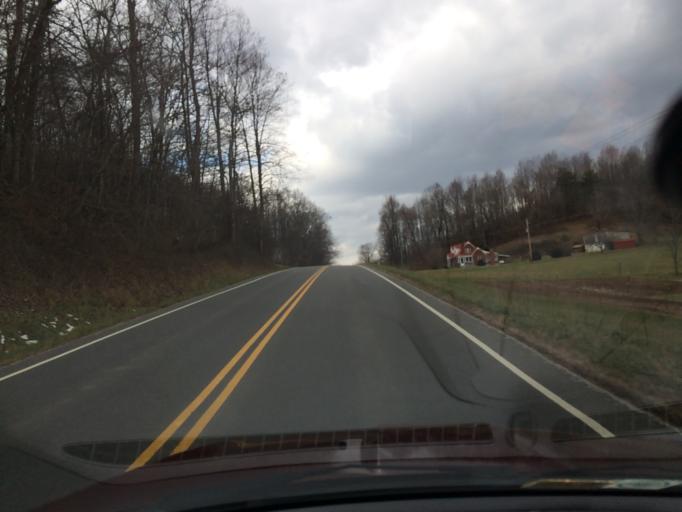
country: US
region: Virginia
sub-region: Patrick County
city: Stuart
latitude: 36.7310
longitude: -80.2450
